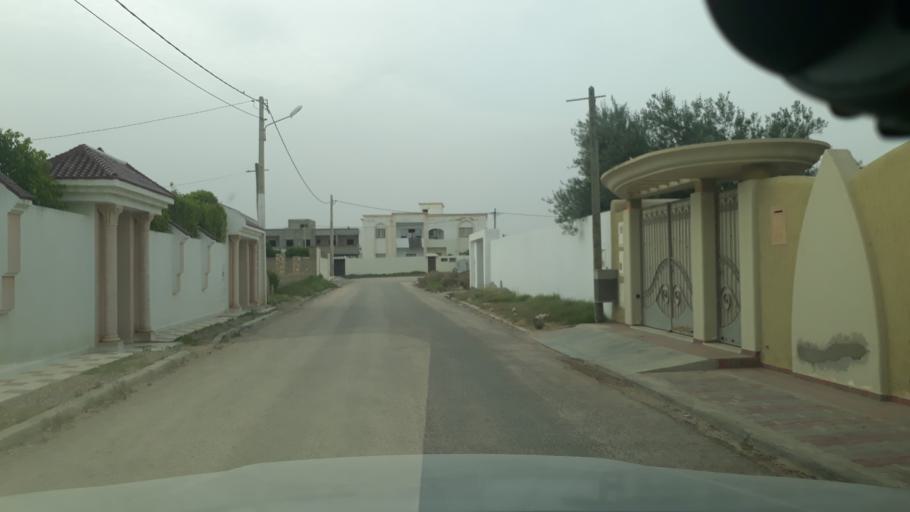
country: TN
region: Safaqis
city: Al Qarmadah
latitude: 34.7791
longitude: 10.7672
